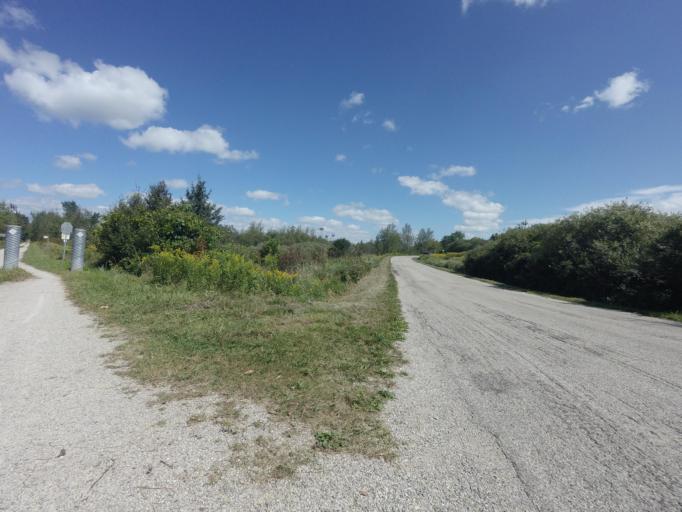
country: CA
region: Ontario
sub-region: Wellington County
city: Guelph
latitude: 43.7465
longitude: -80.3172
